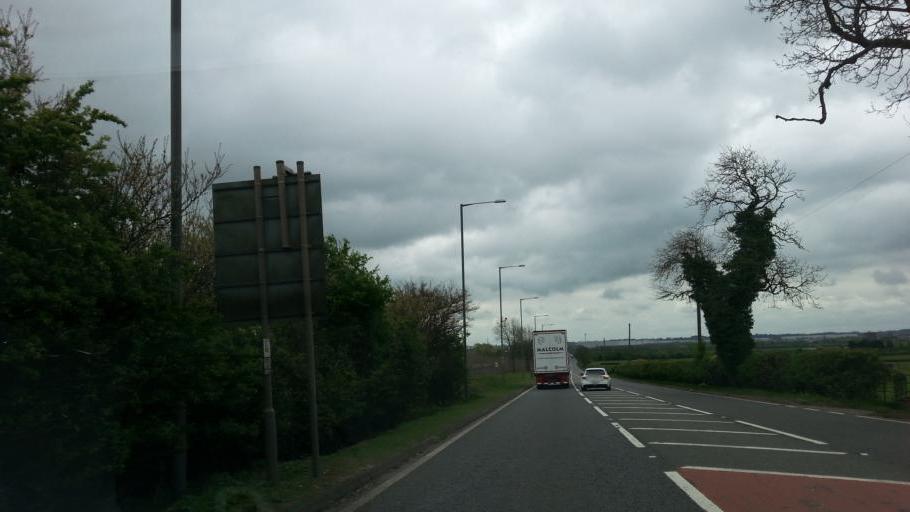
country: GB
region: England
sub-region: Leicestershire
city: Lutterworth
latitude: 52.3842
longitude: -1.1918
